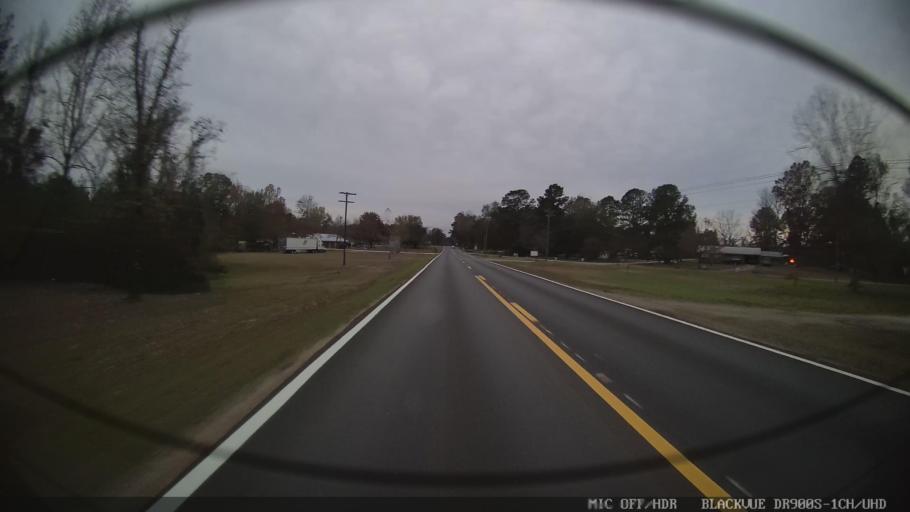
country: US
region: Mississippi
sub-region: Clarke County
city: Quitman
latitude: 32.0530
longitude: -88.6882
